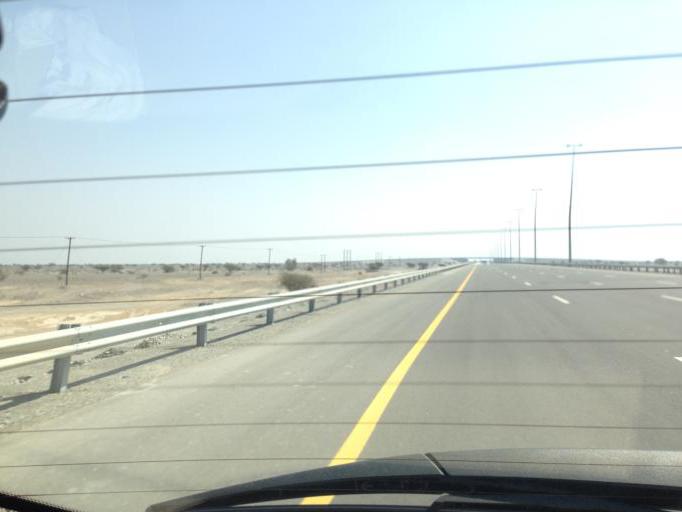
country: OM
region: Al Batinah
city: Barka'
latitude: 23.5757
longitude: 57.7579
